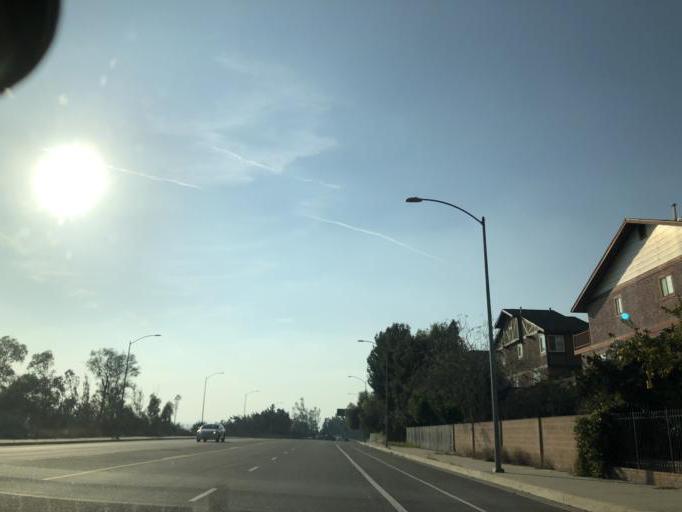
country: US
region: California
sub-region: Los Angeles County
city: Northridge
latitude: 34.2769
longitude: -118.5334
